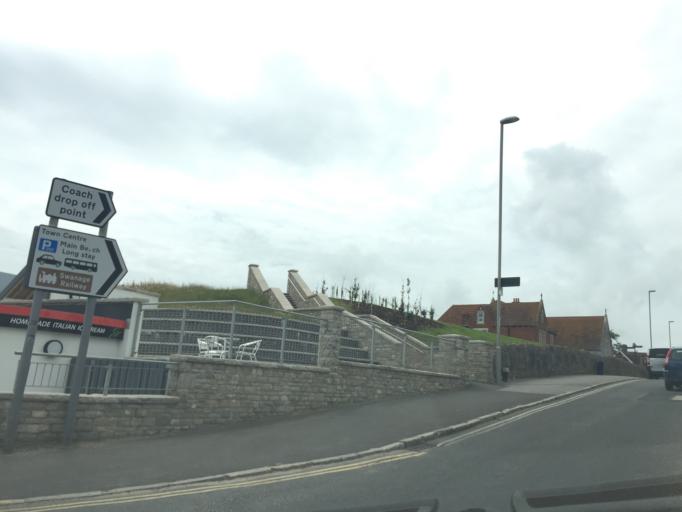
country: GB
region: England
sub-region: Dorset
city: Swanage
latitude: 50.6120
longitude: -1.9579
